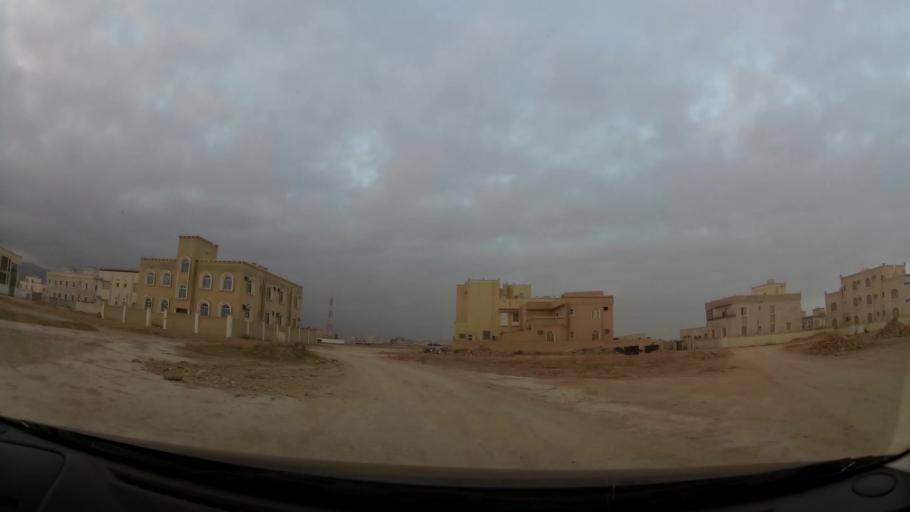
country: OM
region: Zufar
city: Salalah
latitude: 17.0352
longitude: 54.0246
